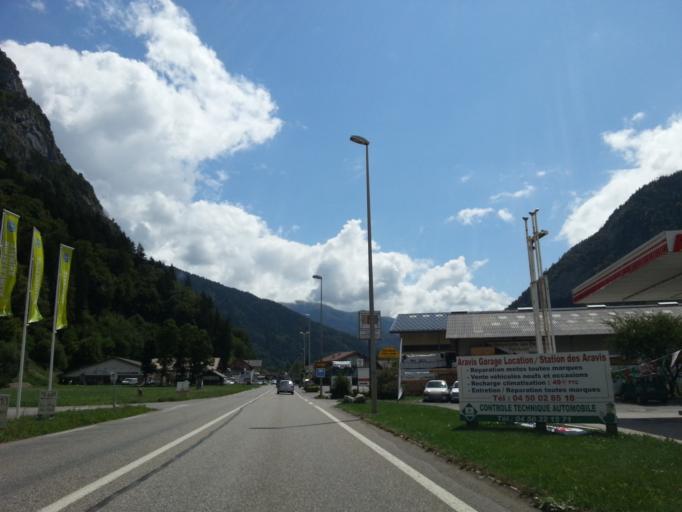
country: FR
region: Rhone-Alpes
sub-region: Departement de la Haute-Savoie
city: Thones
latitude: 45.8902
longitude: 6.3111
